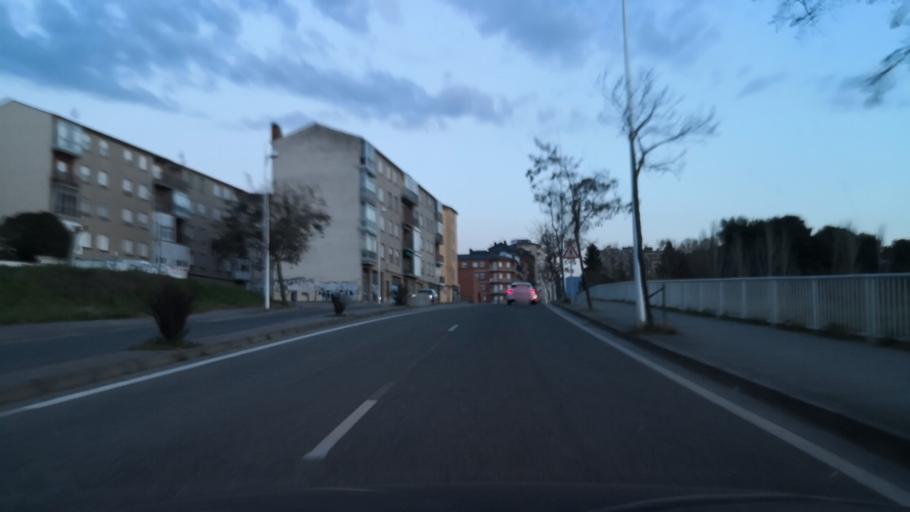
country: ES
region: Castille and Leon
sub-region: Provincia de Leon
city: Ponferrada
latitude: 42.5530
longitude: -6.5855
